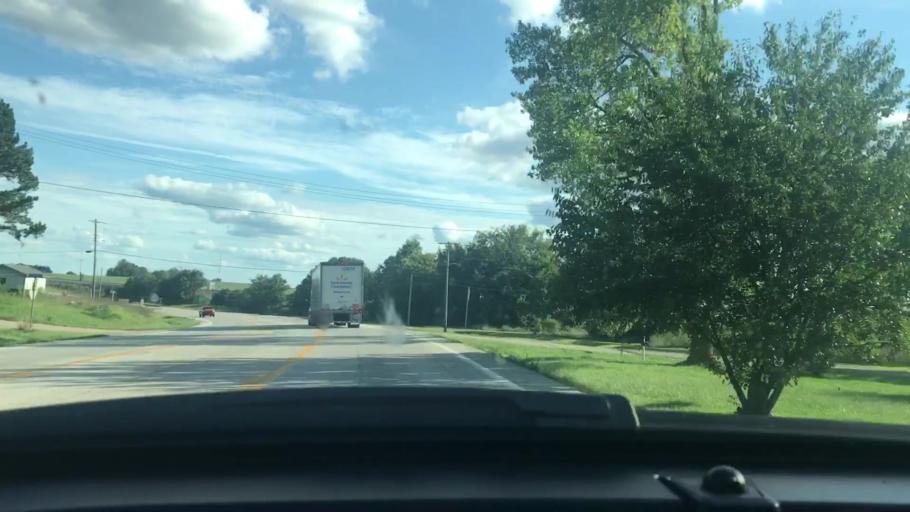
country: US
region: Missouri
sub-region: Oregon County
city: Thayer
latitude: 36.5937
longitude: -91.6439
